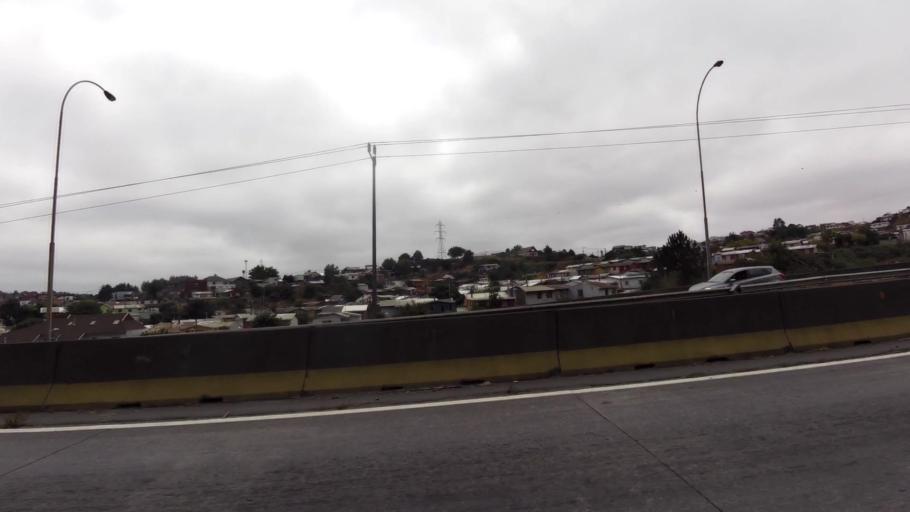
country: CL
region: Biobio
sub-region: Provincia de Concepcion
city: Concepcion
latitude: -36.7990
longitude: -73.0471
